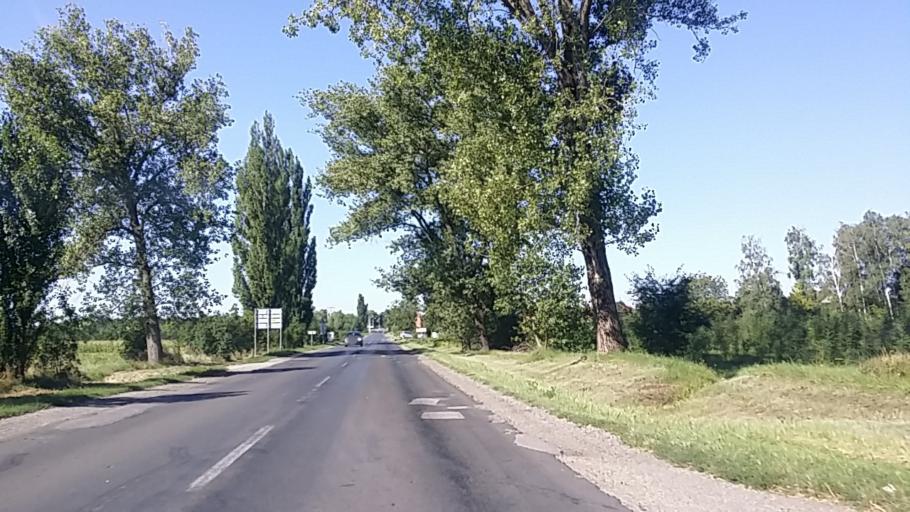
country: HU
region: Fejer
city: Mezofalva
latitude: 46.9317
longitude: 18.7921
